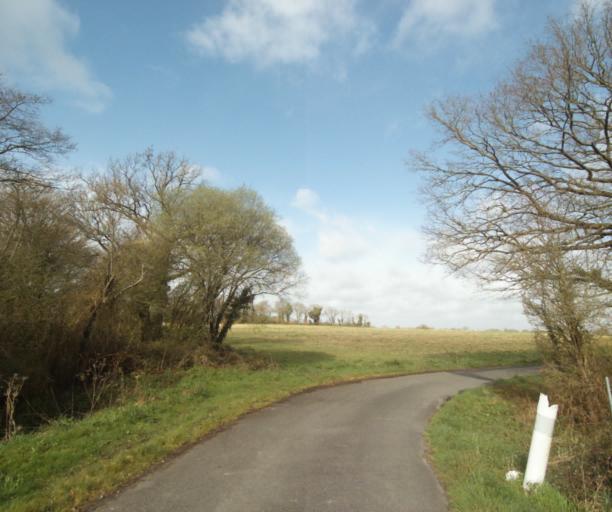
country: FR
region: Pays de la Loire
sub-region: Departement de la Loire-Atlantique
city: Bouvron
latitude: 47.4129
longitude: -1.8661
